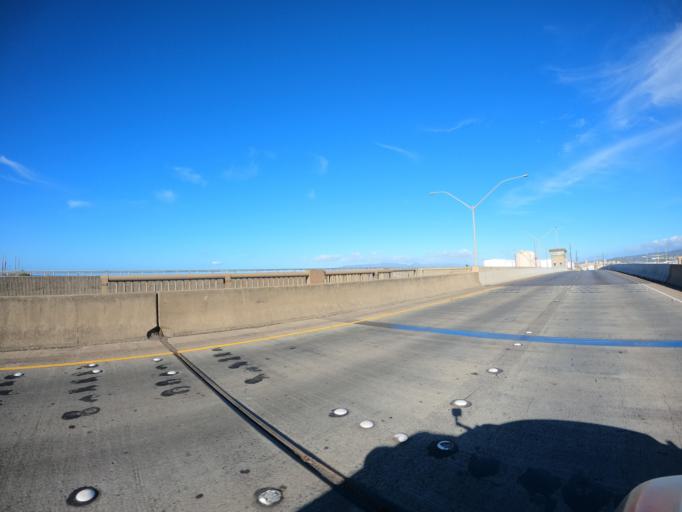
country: US
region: Hawaii
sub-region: Honolulu County
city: Honolulu
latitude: 21.3140
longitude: -157.8877
